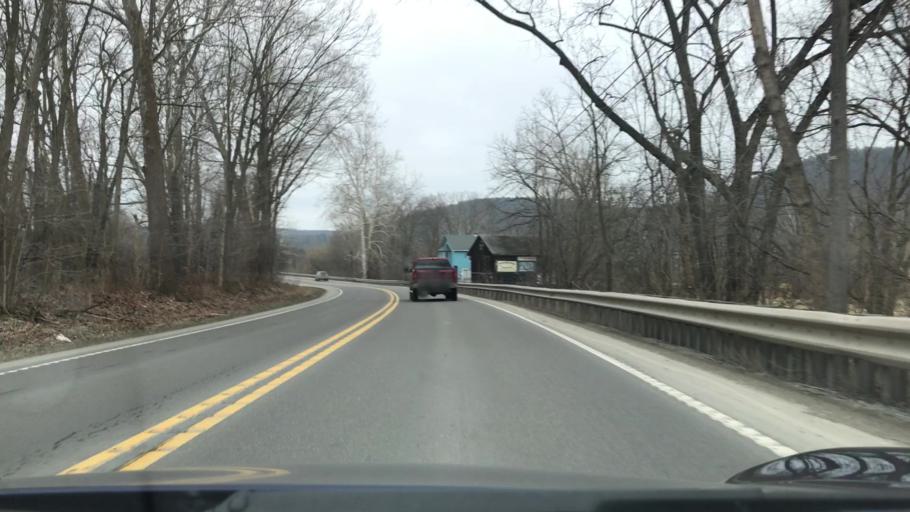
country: US
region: Pennsylvania
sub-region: Bradford County
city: Towanda
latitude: 41.7783
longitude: -76.3829
